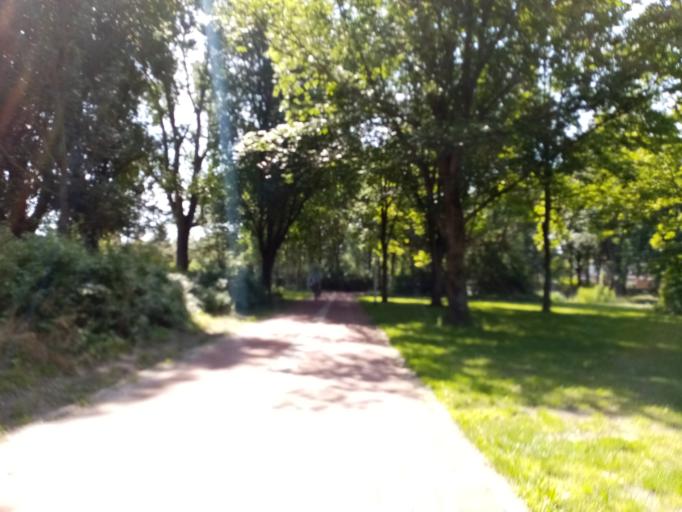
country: NL
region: South Holland
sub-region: Gemeente Katwijk
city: Katwijk aan den Rijn
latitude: 52.2120
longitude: 4.4203
